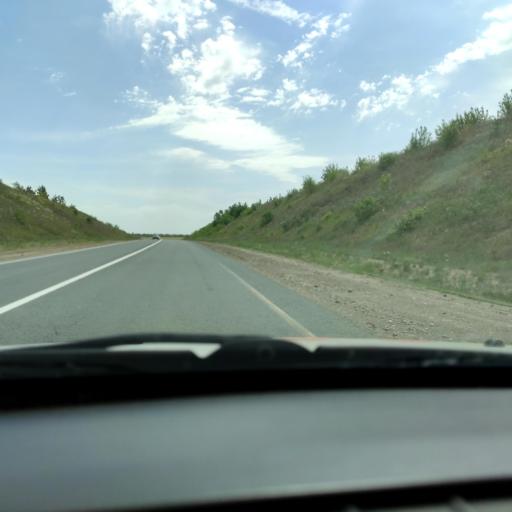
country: RU
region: Samara
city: Mirnyy
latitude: 53.5991
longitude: 50.2763
